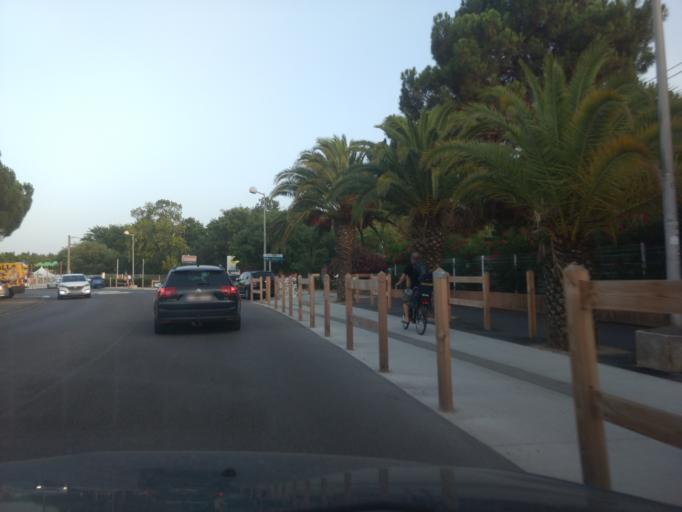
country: FR
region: Languedoc-Roussillon
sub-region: Departement des Pyrenees-Orientales
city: Argelers
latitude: 42.5536
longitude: 3.0432
